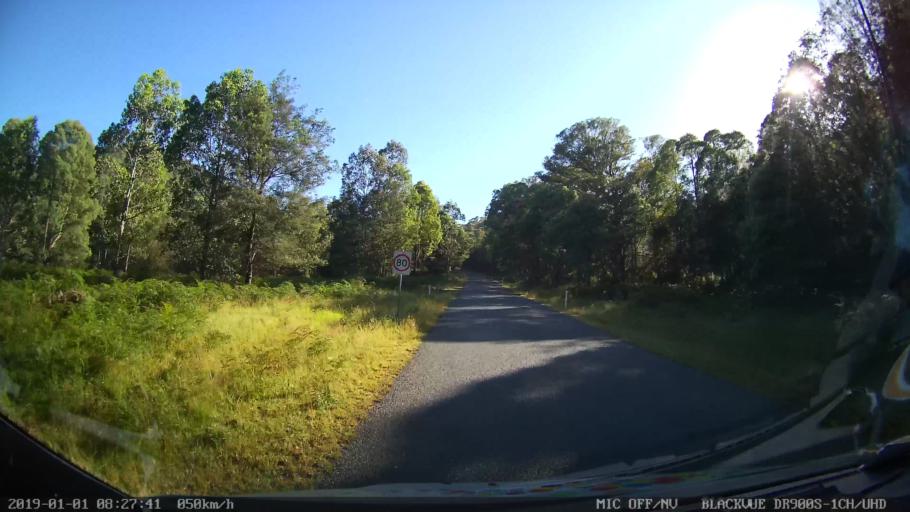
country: AU
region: New South Wales
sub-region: Snowy River
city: Jindabyne
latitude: -36.3799
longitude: 148.1851
